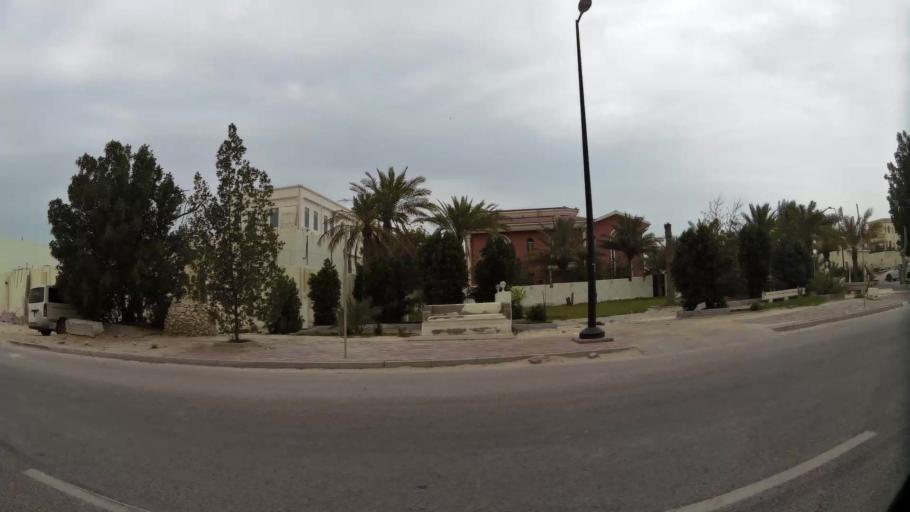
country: QA
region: Baladiyat ad Dawhah
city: Doha
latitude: 25.3485
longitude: 51.4999
